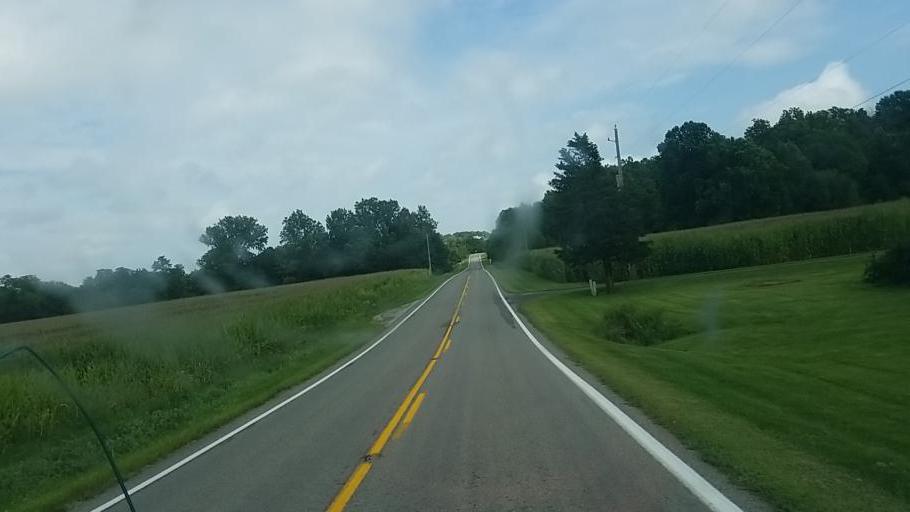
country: US
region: Ohio
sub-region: Champaign County
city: North Lewisburg
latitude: 40.2601
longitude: -83.6433
